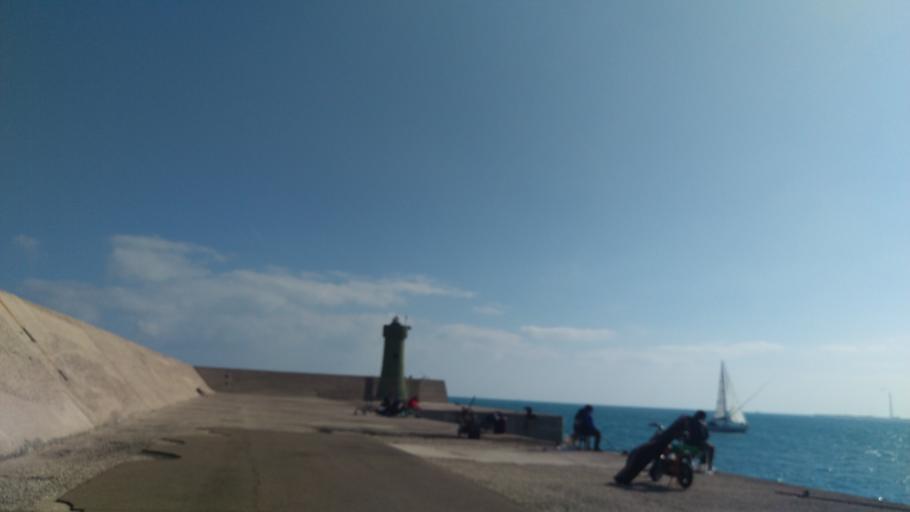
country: IT
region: Apulia
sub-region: Provincia di Brindisi
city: Materdomini
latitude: 40.6632
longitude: 17.9953
